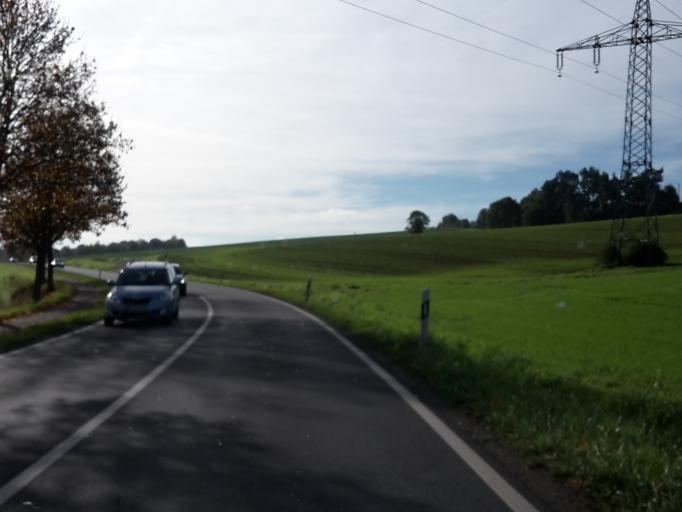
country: DE
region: Hesse
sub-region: Regierungsbezirk Darmstadt
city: Idstein
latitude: 50.2361
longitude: 8.2583
